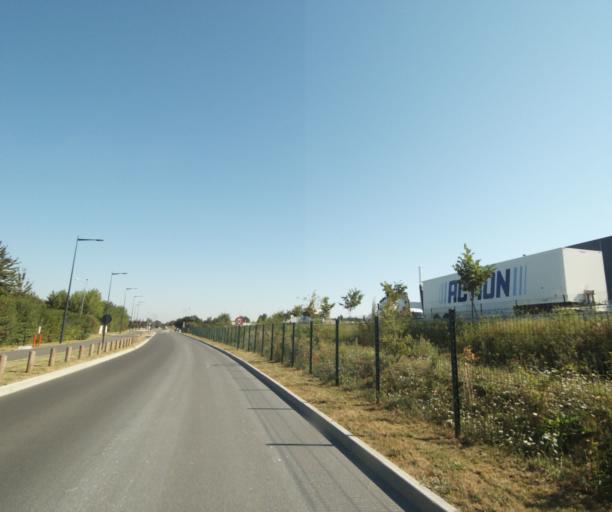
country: FR
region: Ile-de-France
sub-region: Departement de Seine-et-Marne
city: Moissy-Cramayel
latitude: 48.6165
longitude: 2.5815
